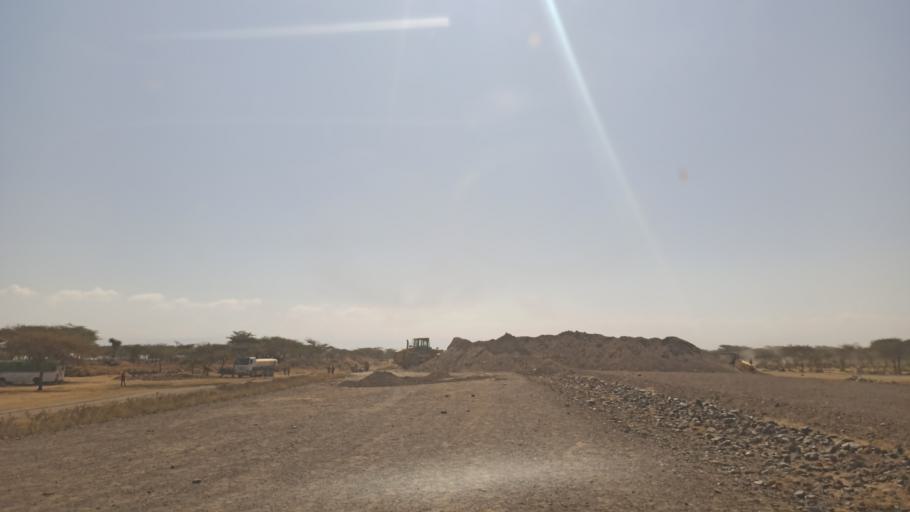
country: ET
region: Oromiya
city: Ziway
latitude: 7.6778
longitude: 38.6759
